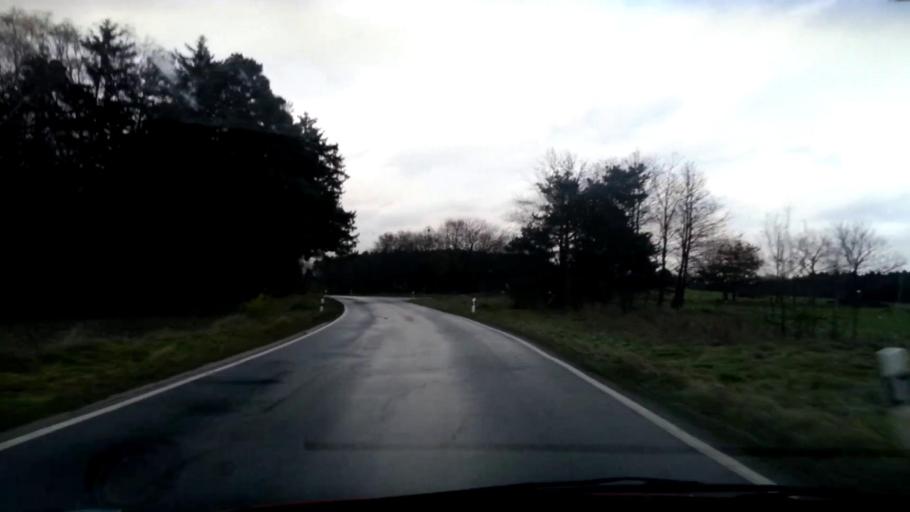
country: DE
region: Bavaria
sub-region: Upper Franconia
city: Aufsess
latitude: 49.9255
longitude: 11.1953
